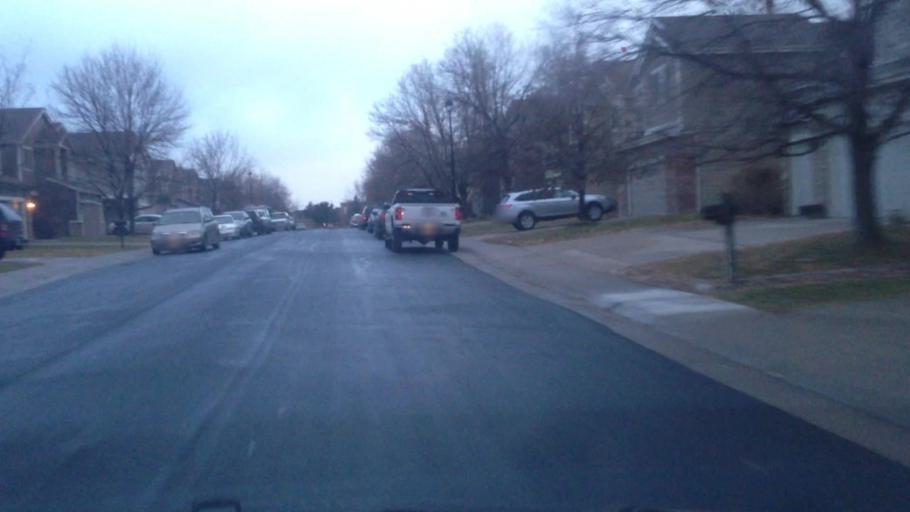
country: US
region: Colorado
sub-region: Douglas County
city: Stonegate
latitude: 39.5175
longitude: -104.7909
